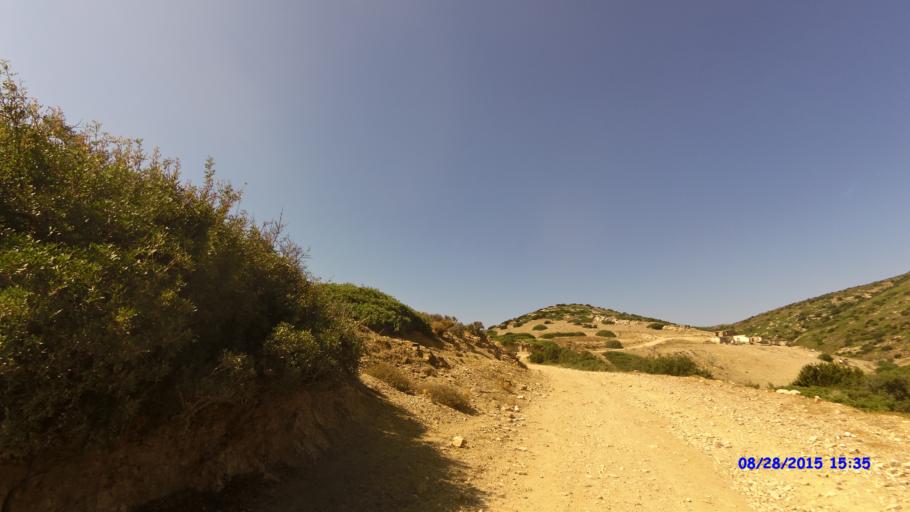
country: GR
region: South Aegean
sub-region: Nomos Kykladon
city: Antiparos
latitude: 36.9832
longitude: 25.0290
